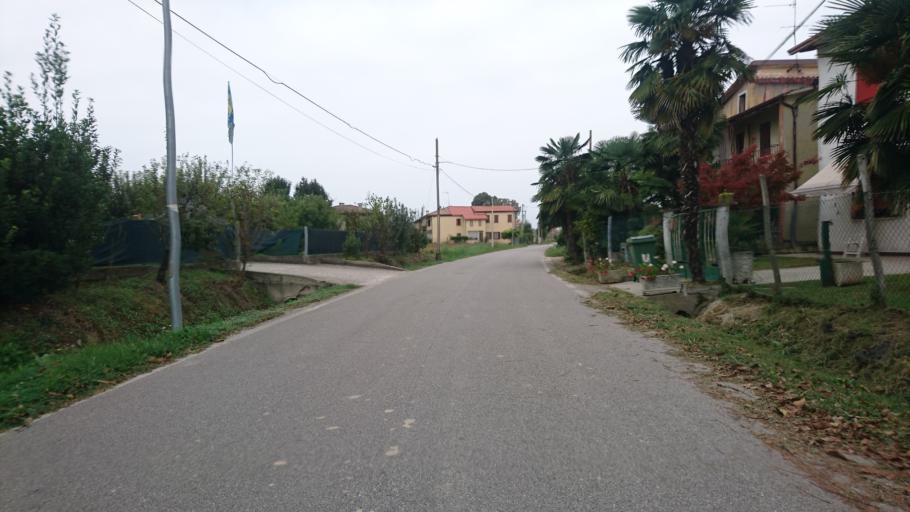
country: IT
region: Veneto
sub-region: Provincia di Padova
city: Santa Maria di Non
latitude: 45.5198
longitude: 11.8513
